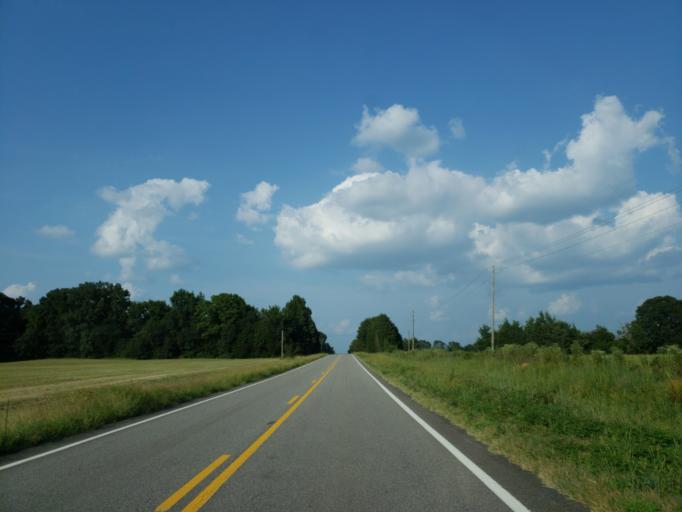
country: US
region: Alabama
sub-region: Greene County
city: Eutaw
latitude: 32.7640
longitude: -88.0047
